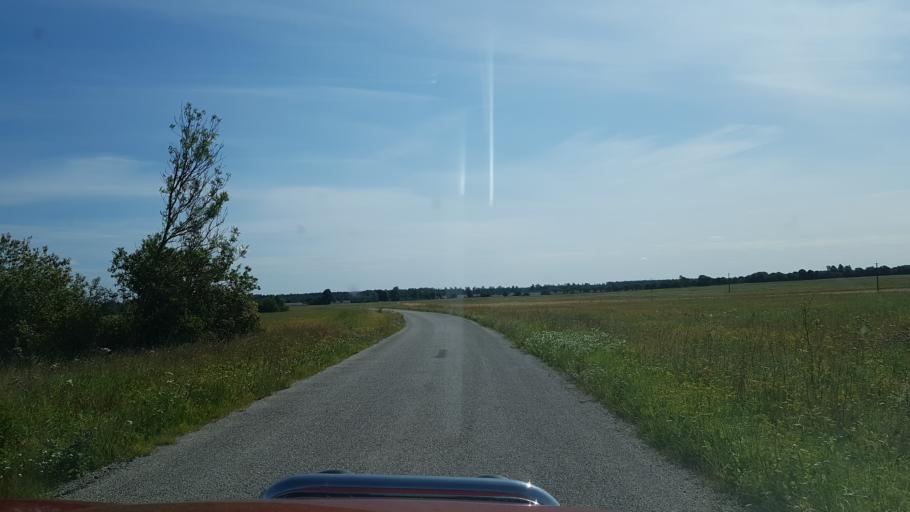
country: EE
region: Jaervamaa
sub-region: Jaerva-Jaani vald
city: Jarva-Jaani
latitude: 59.0877
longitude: 25.7378
